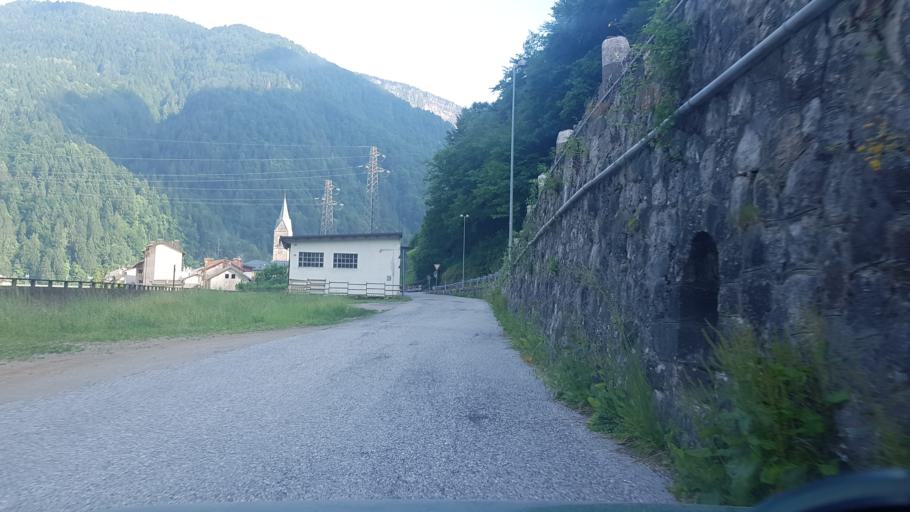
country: IT
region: Friuli Venezia Giulia
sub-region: Provincia di Udine
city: Pontebba
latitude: 46.5090
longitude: 13.3006
